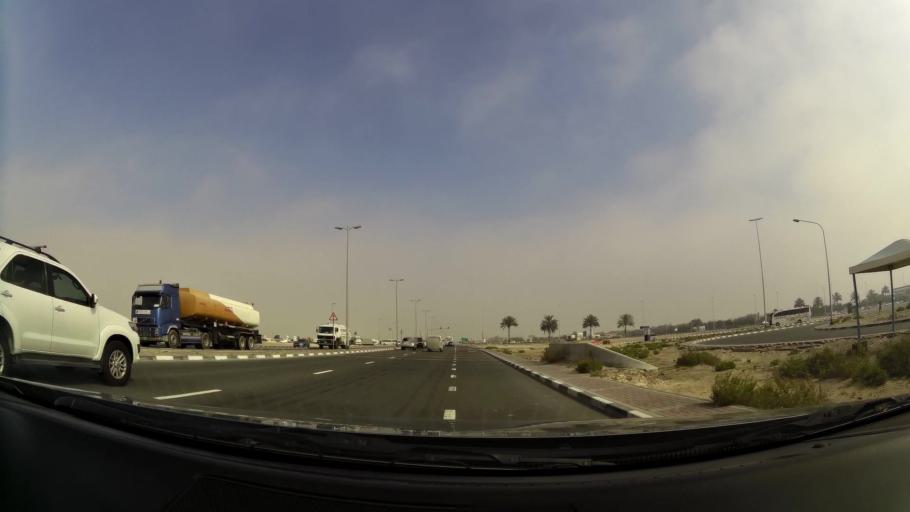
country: AE
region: Dubai
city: Dubai
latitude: 24.9570
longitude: 55.0520
